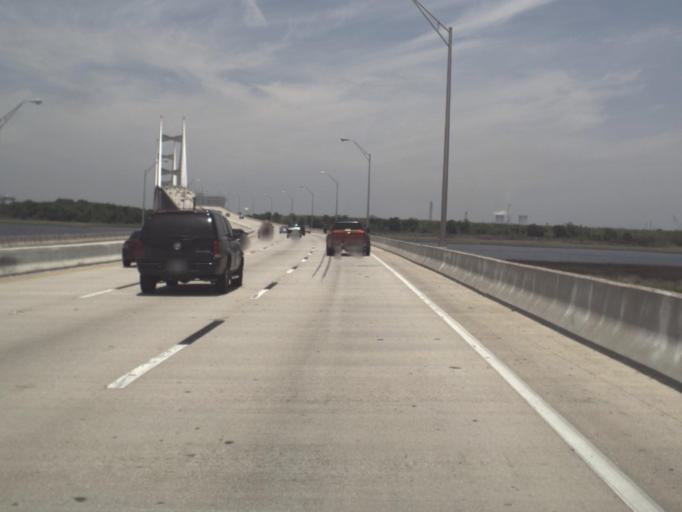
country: US
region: Florida
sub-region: Duval County
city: Jacksonville
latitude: 30.3715
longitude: -81.5517
